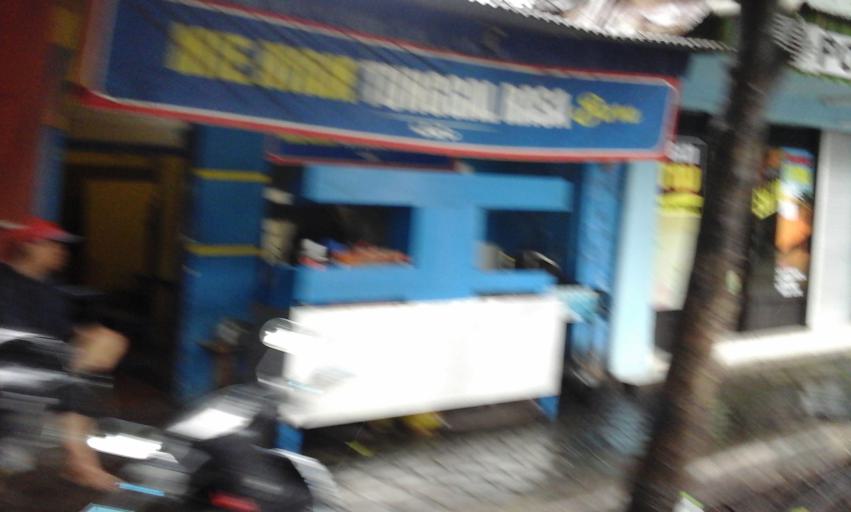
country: ID
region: East Java
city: Lumajang
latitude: -8.1283
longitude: 113.2235
